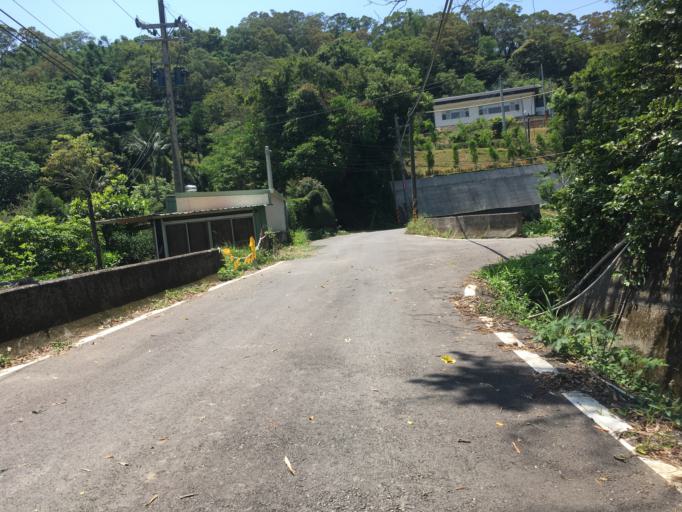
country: TW
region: Taiwan
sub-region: Hsinchu
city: Hsinchu
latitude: 24.7306
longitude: 120.9813
